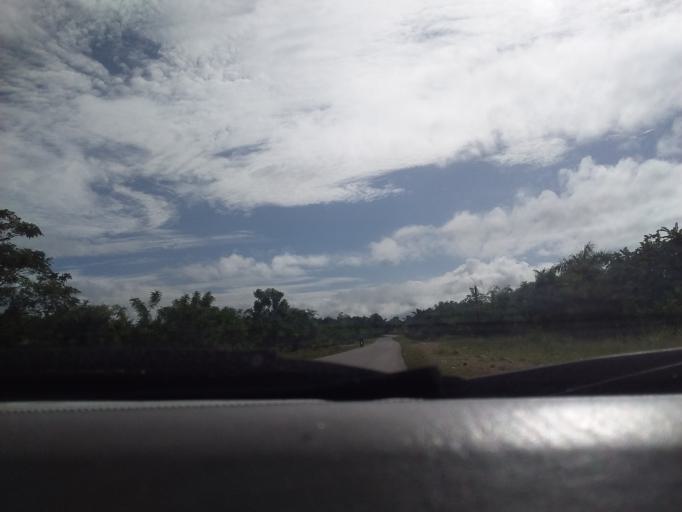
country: DO
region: Santo Domingo
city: Guerra
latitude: 18.5596
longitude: -69.7872
